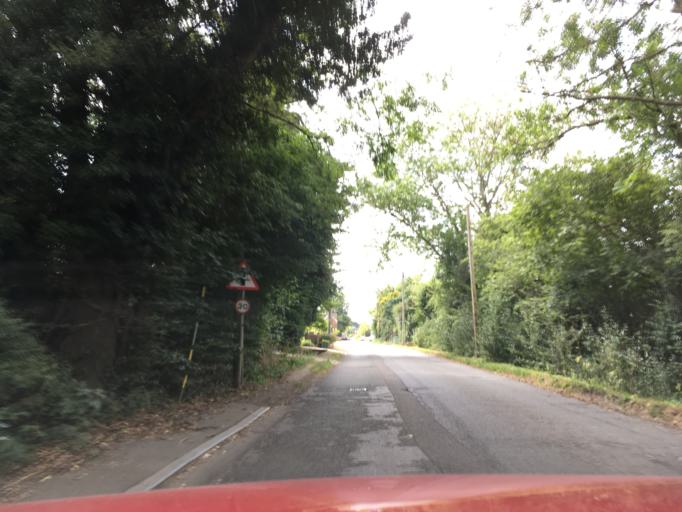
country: GB
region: England
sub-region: Kent
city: Staplehurst
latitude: 51.2235
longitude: 0.5735
